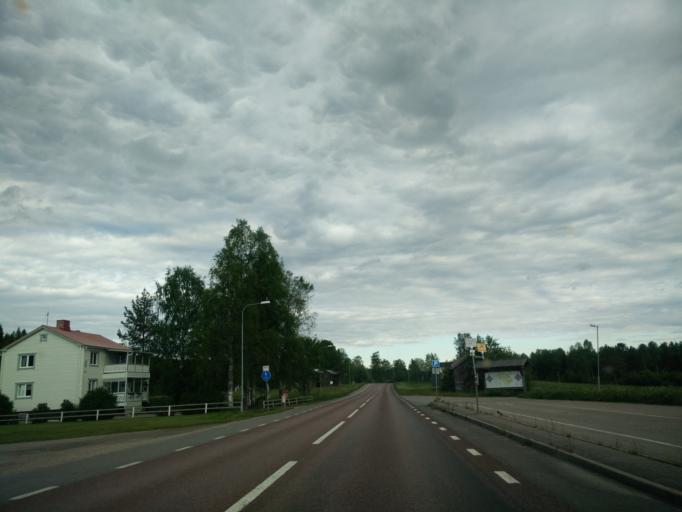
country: SE
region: Jaemtland
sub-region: Harjedalens Kommun
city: Sveg
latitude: 62.2814
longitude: 14.8031
